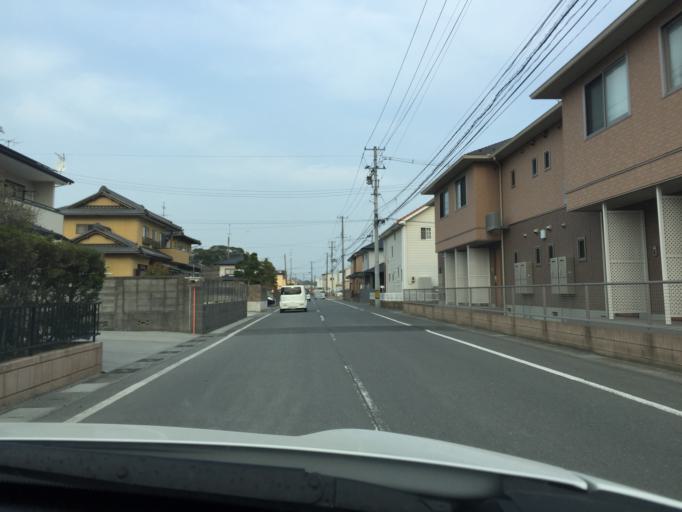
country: JP
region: Fukushima
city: Iwaki
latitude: 37.0700
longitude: 140.9400
